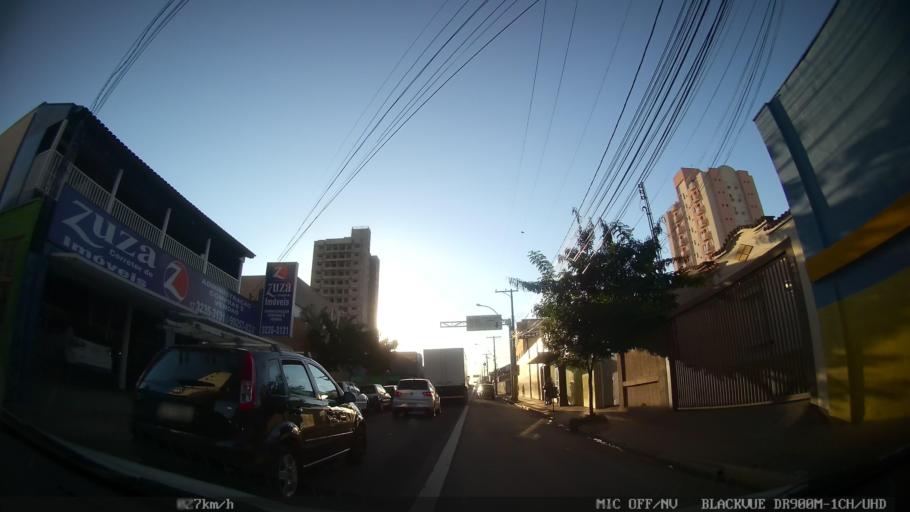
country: BR
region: Sao Paulo
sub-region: Sao Jose Do Rio Preto
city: Sao Jose do Rio Preto
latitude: -20.8052
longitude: -49.3818
